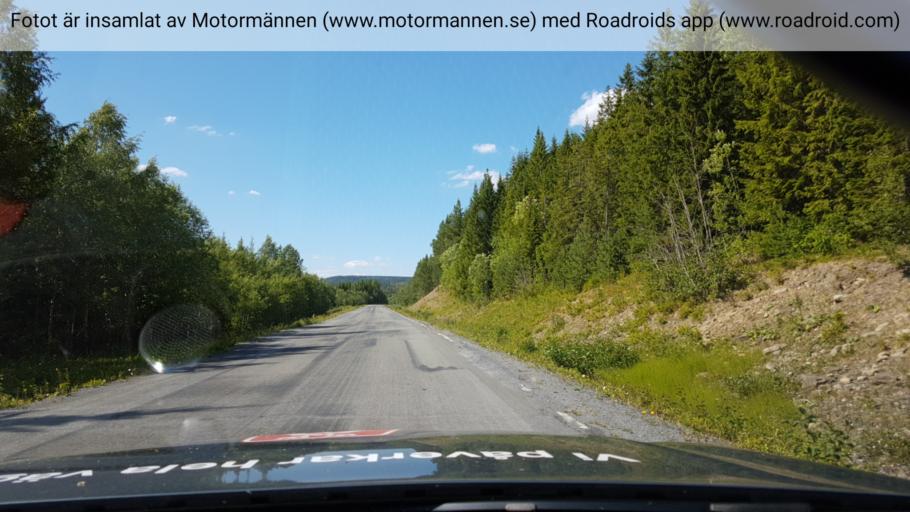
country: SE
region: Jaemtland
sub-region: Are Kommun
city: Jarpen
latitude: 63.2981
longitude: 13.7057
